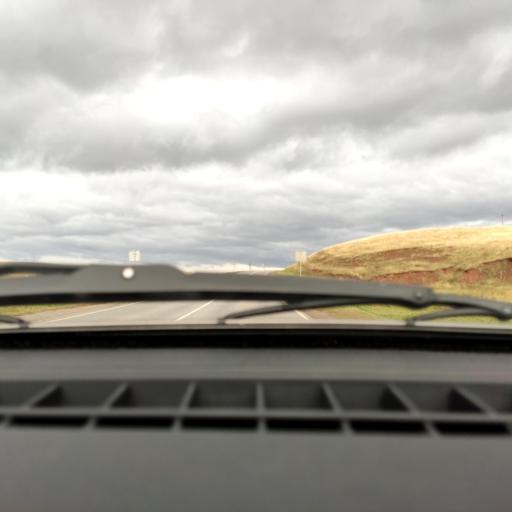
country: RU
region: Bashkortostan
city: Rayevskiy
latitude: 54.0166
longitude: 54.8778
